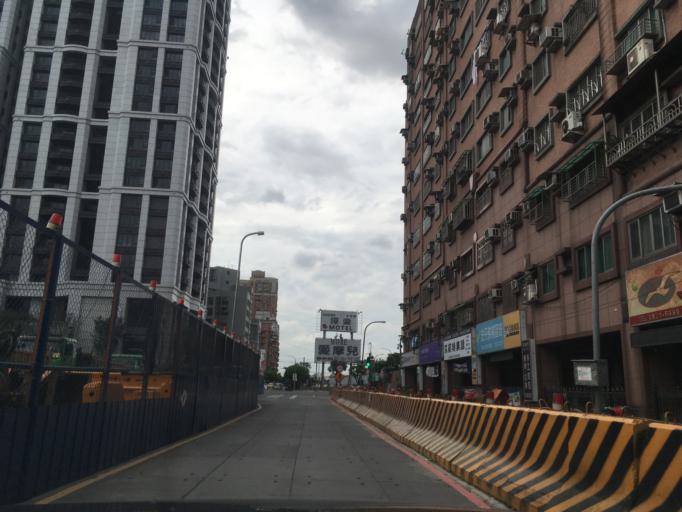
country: TW
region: Taipei
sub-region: Taipei
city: Banqiao
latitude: 25.0086
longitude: 121.5055
